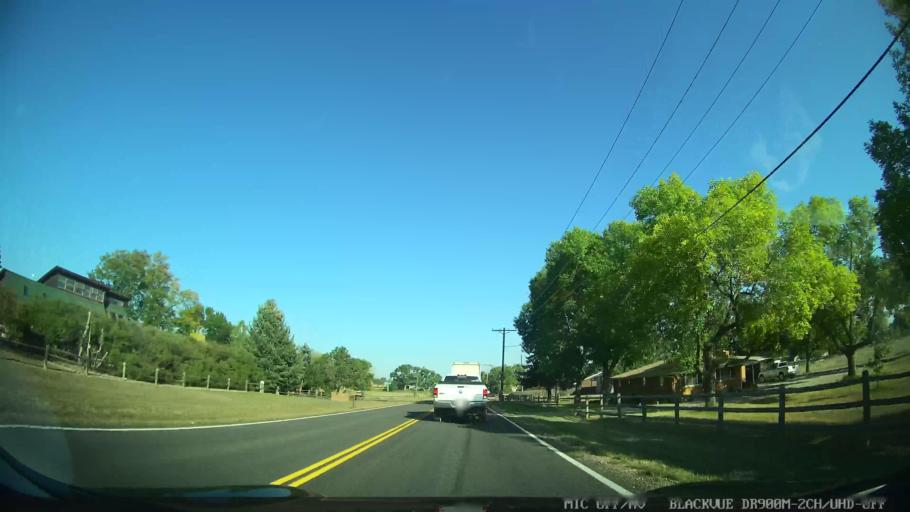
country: US
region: Colorado
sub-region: Larimer County
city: Loveland
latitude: 40.4510
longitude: -105.0622
